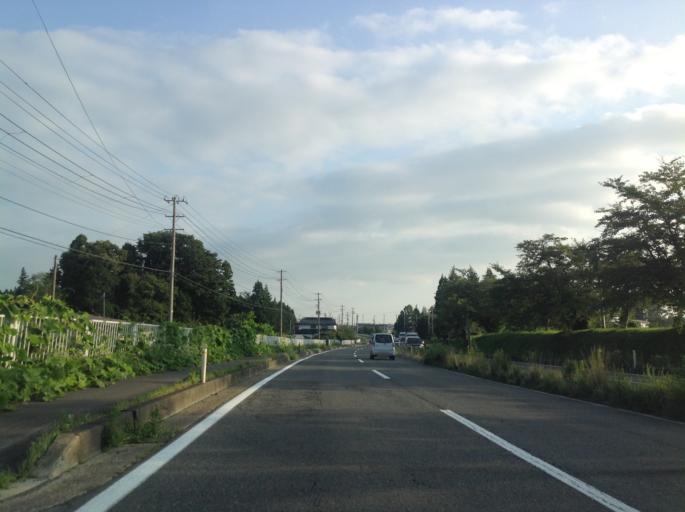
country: JP
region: Iwate
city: Hanamaki
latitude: 39.5314
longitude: 141.1649
